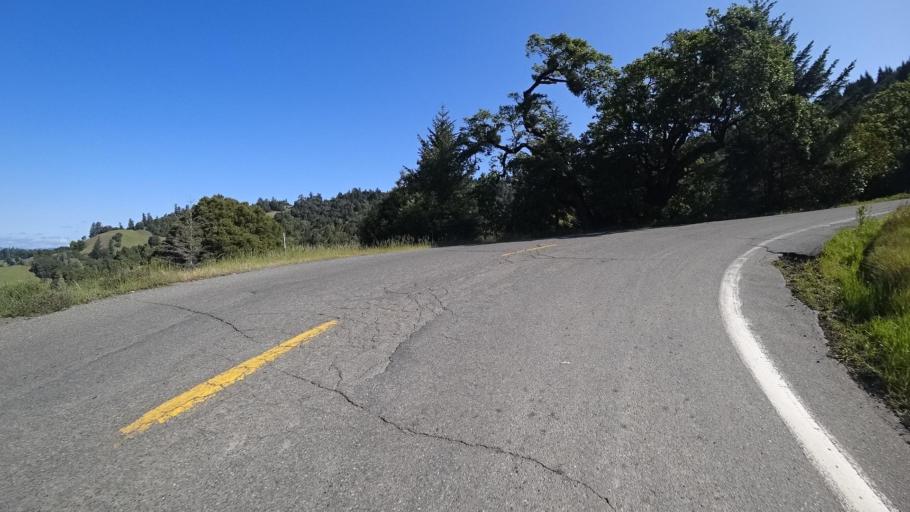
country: US
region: California
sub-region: Humboldt County
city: Redway
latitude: 40.1139
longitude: -123.7738
